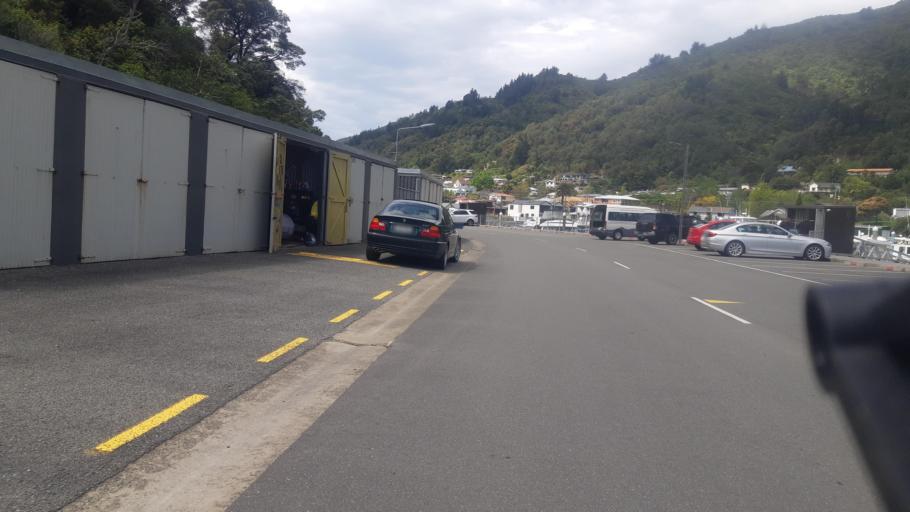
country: NZ
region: Marlborough
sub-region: Marlborough District
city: Picton
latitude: -41.2883
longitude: 174.0116
